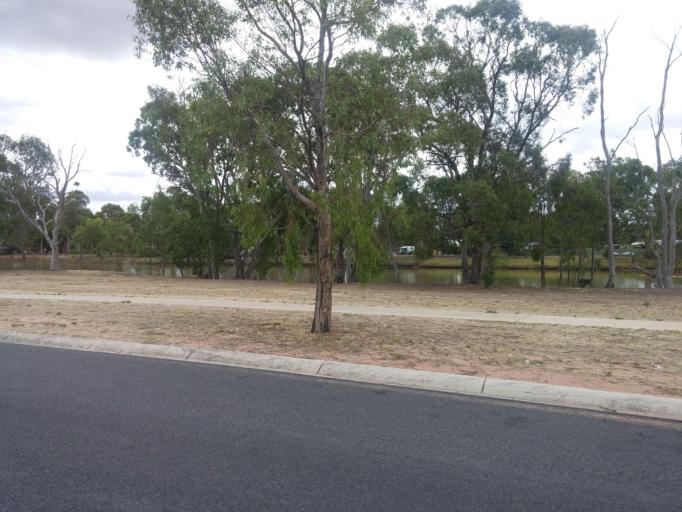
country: AU
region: Victoria
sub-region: Horsham
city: Horsham
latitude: -36.7245
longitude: 142.2002
